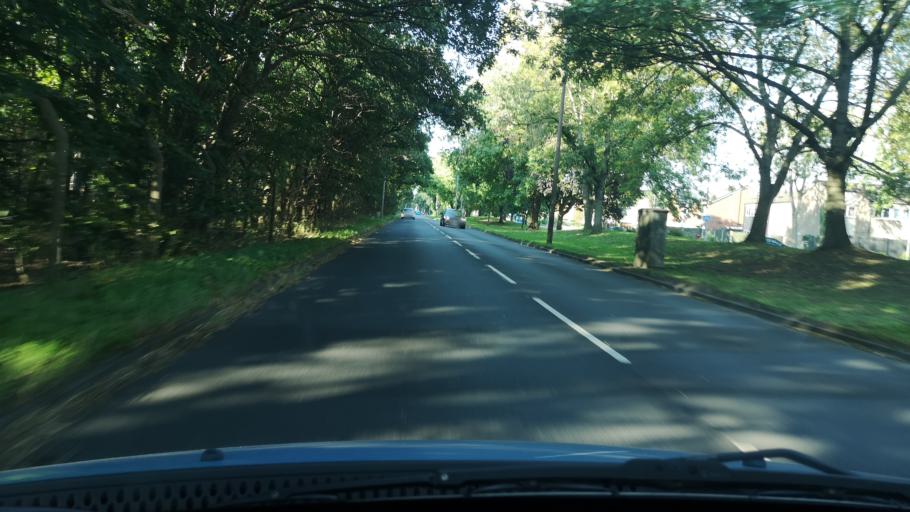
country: GB
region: England
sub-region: North Lincolnshire
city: Scunthorpe
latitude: 53.5783
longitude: -0.6837
